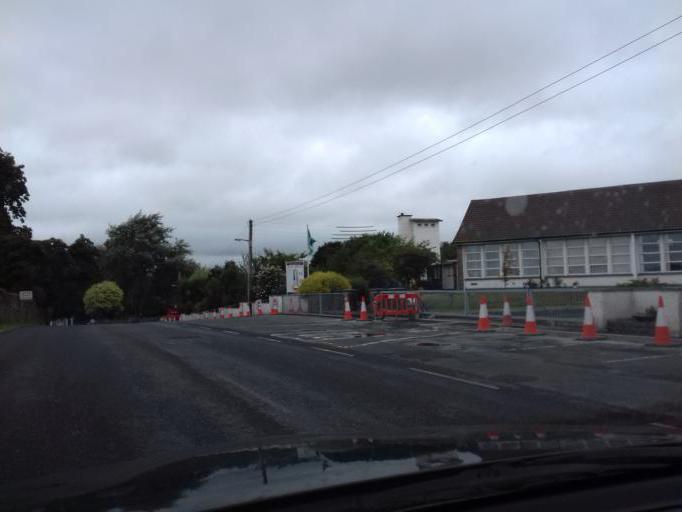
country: IE
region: Leinster
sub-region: County Carlow
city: Bagenalstown
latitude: 52.7349
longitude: -6.9719
